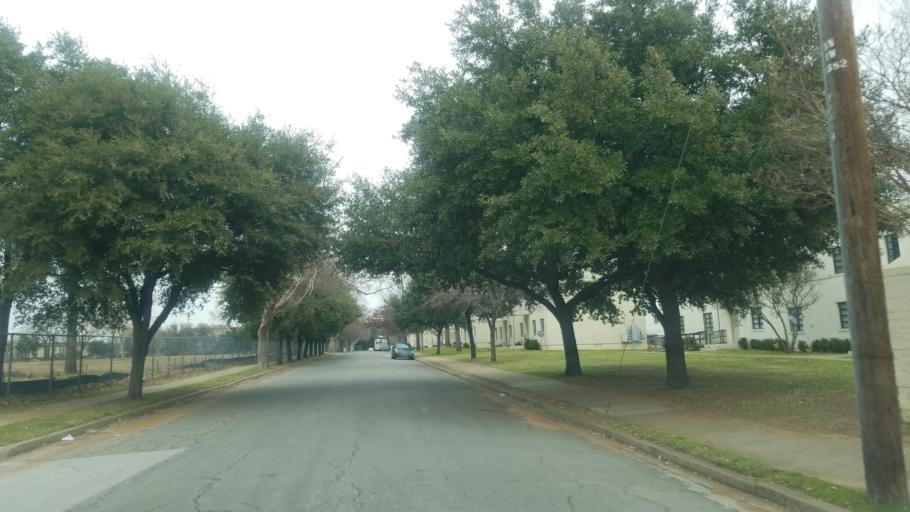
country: US
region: Texas
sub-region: Dallas County
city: Dallas
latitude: 32.8136
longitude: -96.8228
